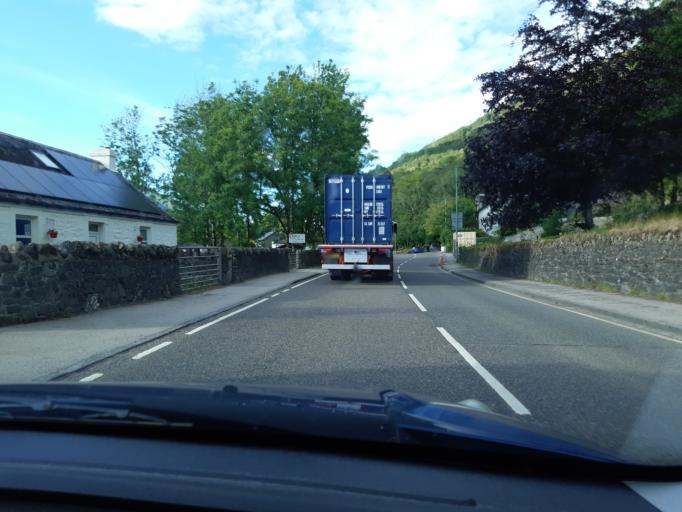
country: GB
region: Scotland
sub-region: Argyll and Bute
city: Garelochhead
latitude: 56.2024
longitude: -4.7446
